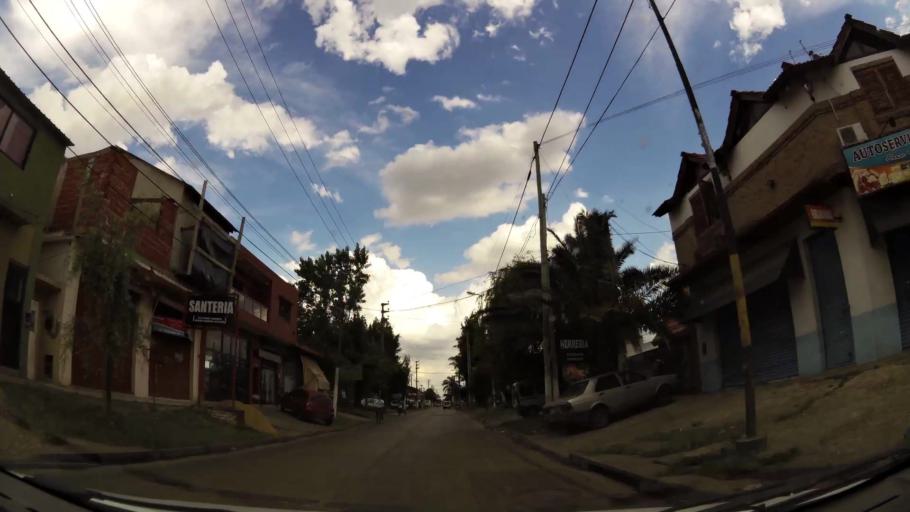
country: AR
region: Buenos Aires
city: Ituzaingo
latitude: -34.6395
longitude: -58.6765
